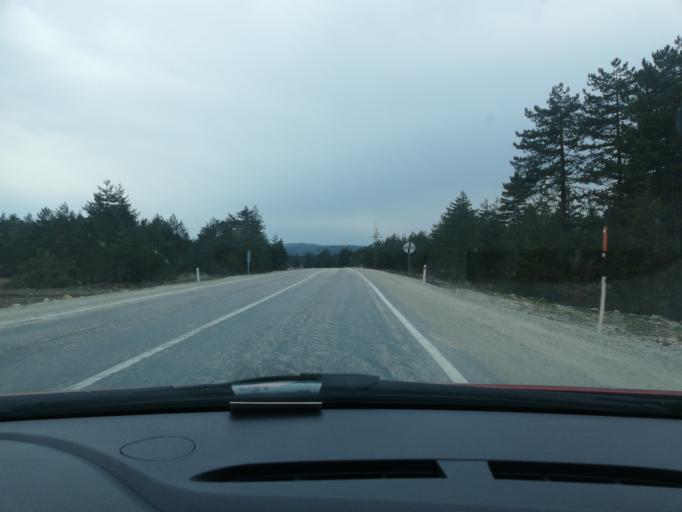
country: TR
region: Karabuk
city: Eflani
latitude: 41.4887
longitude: 33.0394
